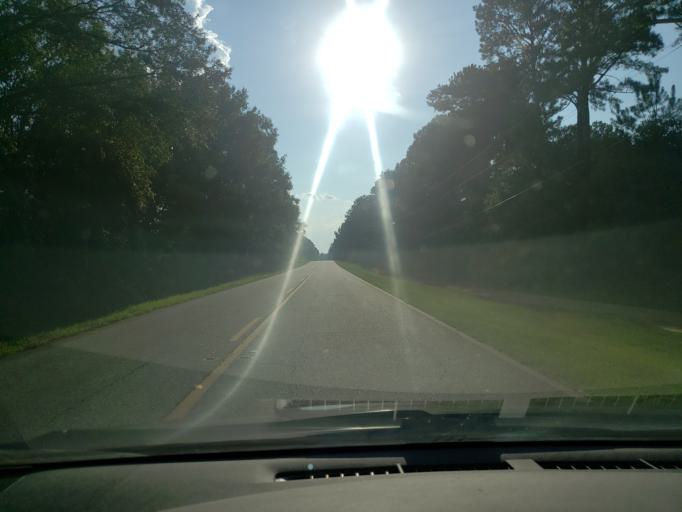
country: US
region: Georgia
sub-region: Terrell County
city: Dawson
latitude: 31.5774
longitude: -84.3809
